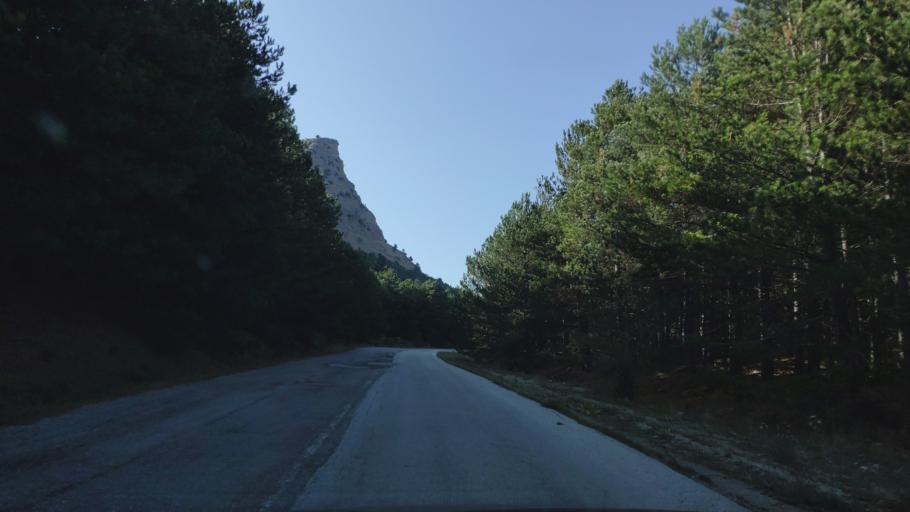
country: GR
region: West Greece
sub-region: Nomos Achaias
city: Aiyira
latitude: 38.0328
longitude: 22.4025
